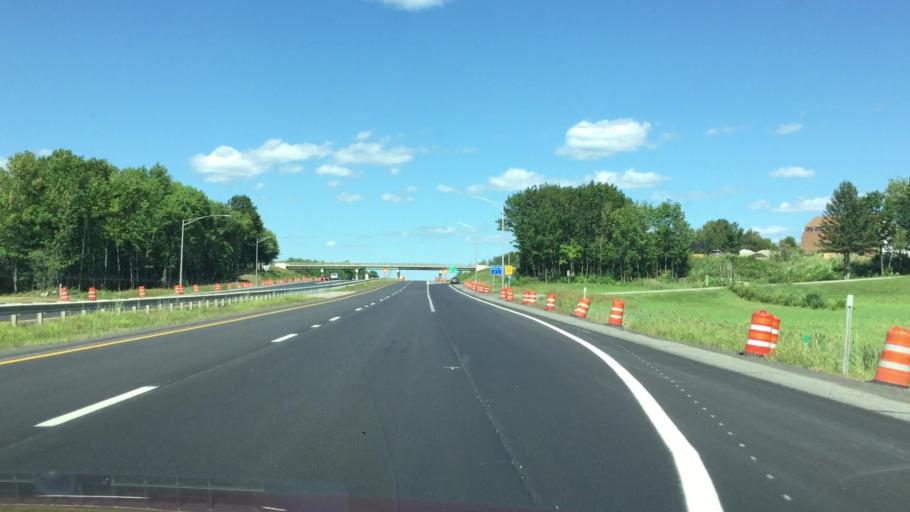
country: US
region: Maine
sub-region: Kennebec County
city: Gardiner
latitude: 44.2088
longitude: -69.8323
